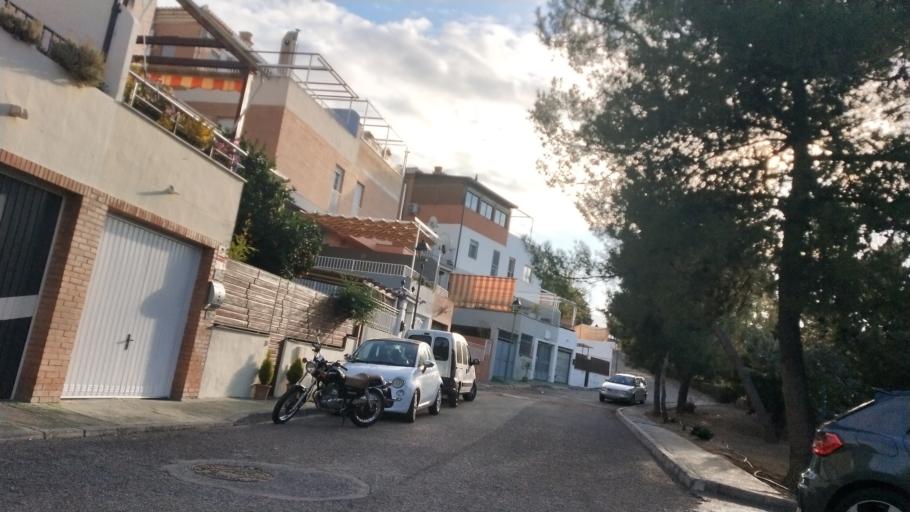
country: ES
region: Andalusia
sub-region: Provincia de Granada
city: Cenes de la Vega
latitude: 37.1677
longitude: -3.5464
